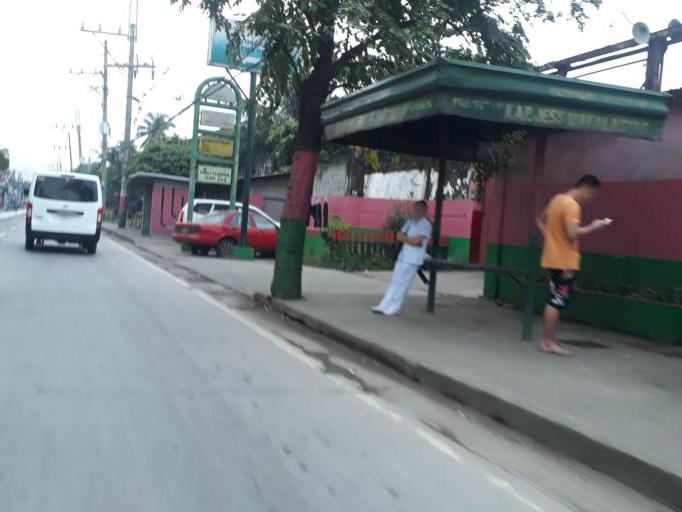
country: PH
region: Calabarzon
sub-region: Province of Rizal
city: Valenzuela
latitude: 14.6938
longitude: 120.9549
